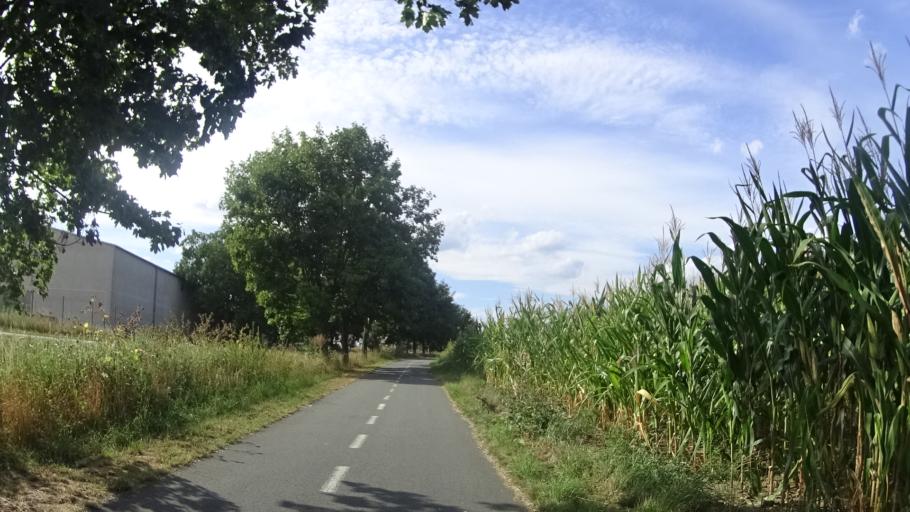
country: CZ
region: Olomoucky
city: Moravicany
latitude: 49.7711
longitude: 16.9426
